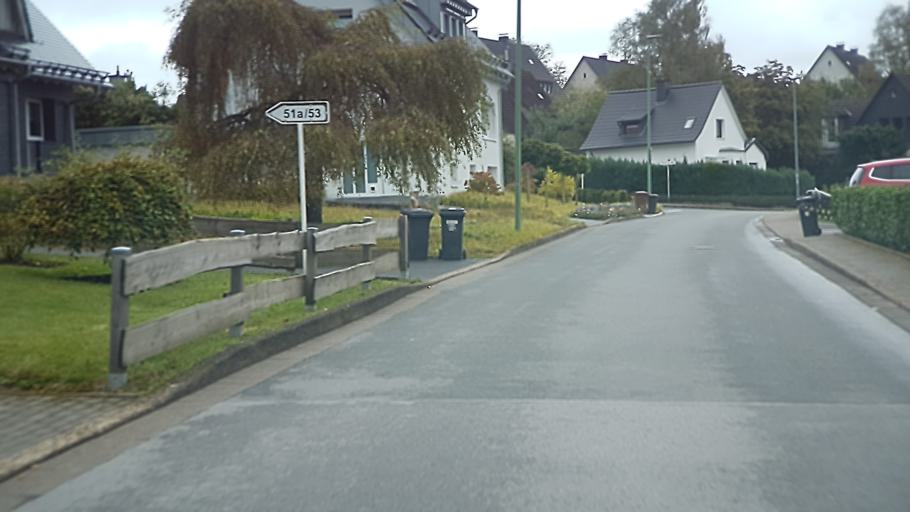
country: DE
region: North Rhine-Westphalia
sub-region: Regierungsbezirk Arnsberg
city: Luedenscheid
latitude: 51.2146
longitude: 7.6630
